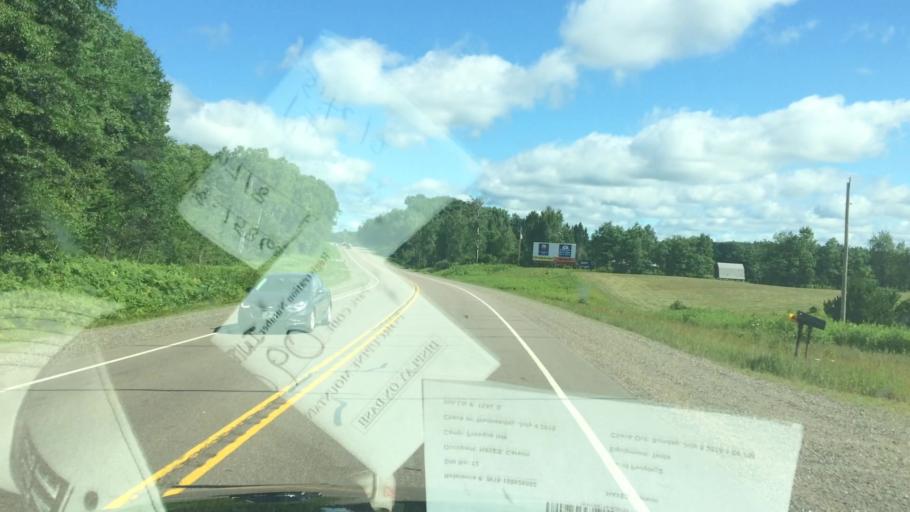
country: US
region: Wisconsin
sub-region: Oneida County
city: Rhinelander
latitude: 45.5766
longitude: -89.5695
